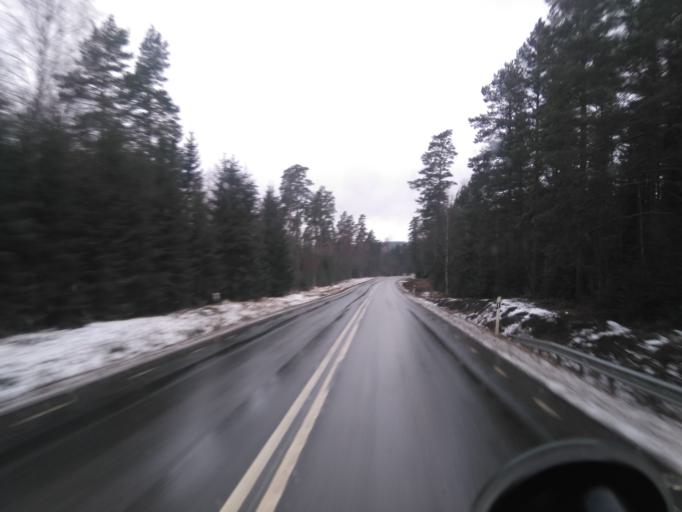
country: SE
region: Joenkoeping
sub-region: Eksjo Kommun
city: Haljarp
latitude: 57.6211
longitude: 15.4656
